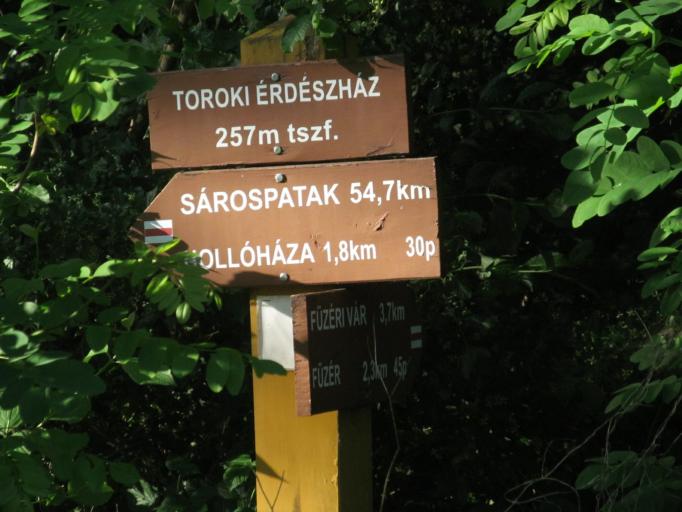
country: HU
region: Borsod-Abauj-Zemplen
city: Gonc
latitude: 48.5257
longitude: 21.4377
